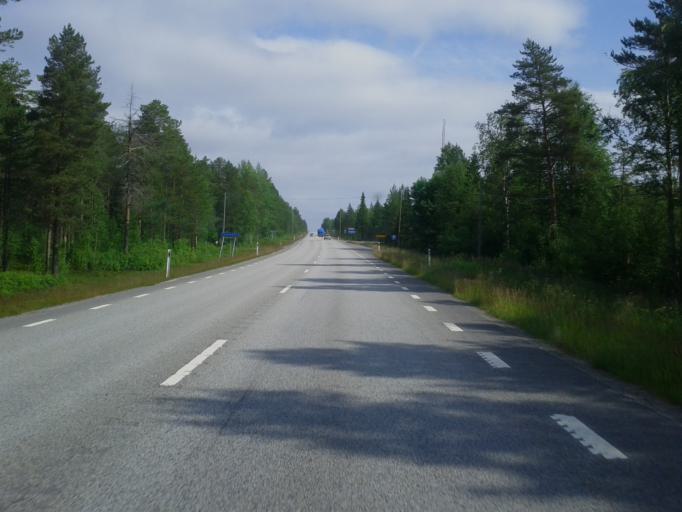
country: SE
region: Vaesterbotten
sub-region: Robertsfors Kommun
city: Robertsfors
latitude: 64.1878
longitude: 20.9961
